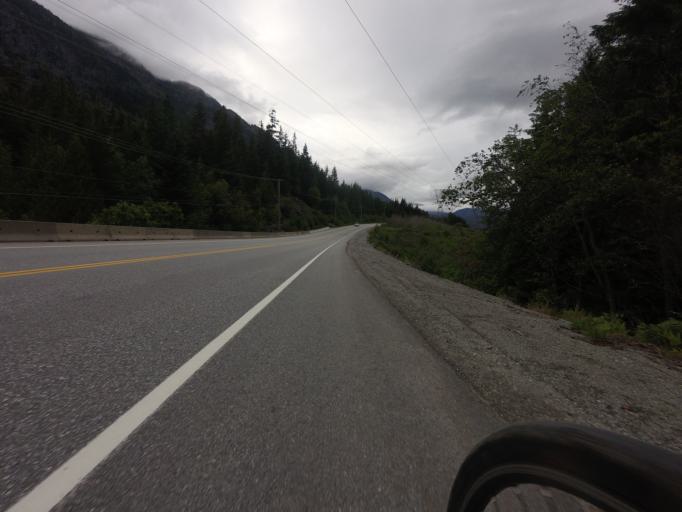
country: CA
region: British Columbia
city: Whistler
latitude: 50.1878
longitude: -122.8758
